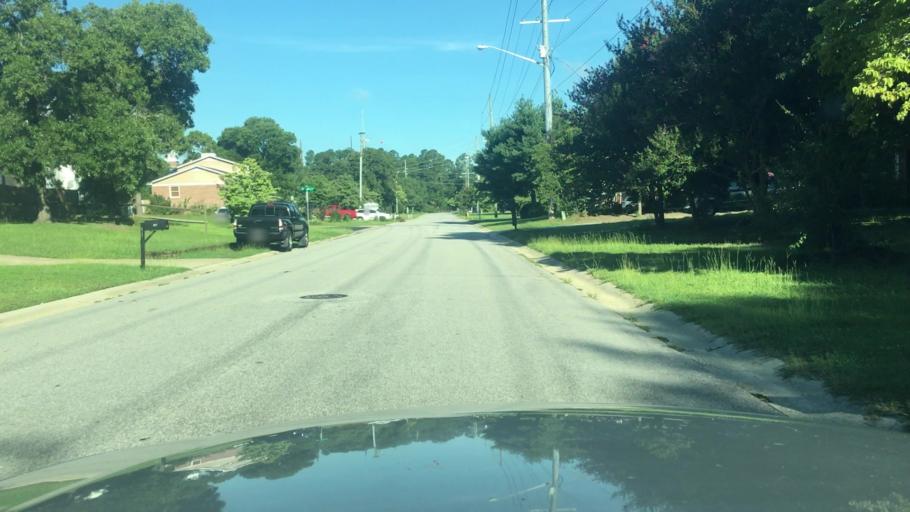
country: US
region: North Carolina
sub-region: Cumberland County
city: Fayetteville
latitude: 35.1308
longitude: -78.8892
